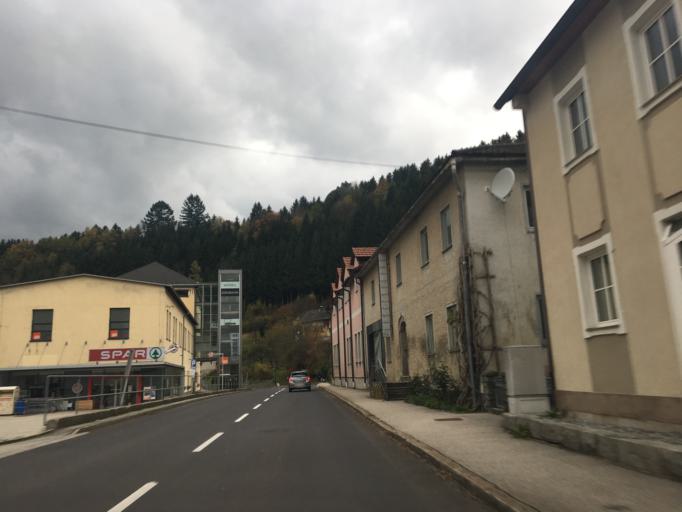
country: AT
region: Upper Austria
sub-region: Politischer Bezirk Urfahr-Umgebung
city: Herzogsdorf
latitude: 48.5422
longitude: 14.1413
